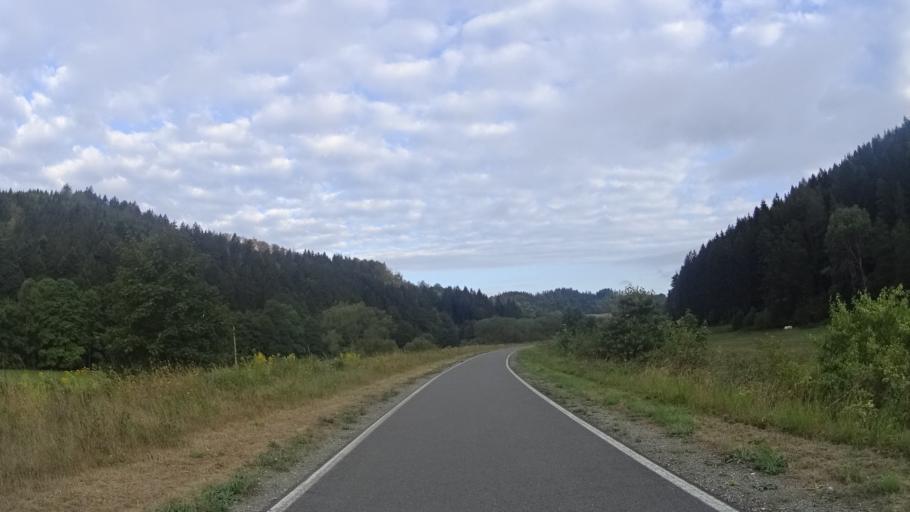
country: CZ
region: Olomoucky
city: Zabreh
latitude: 49.8590
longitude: 16.8232
